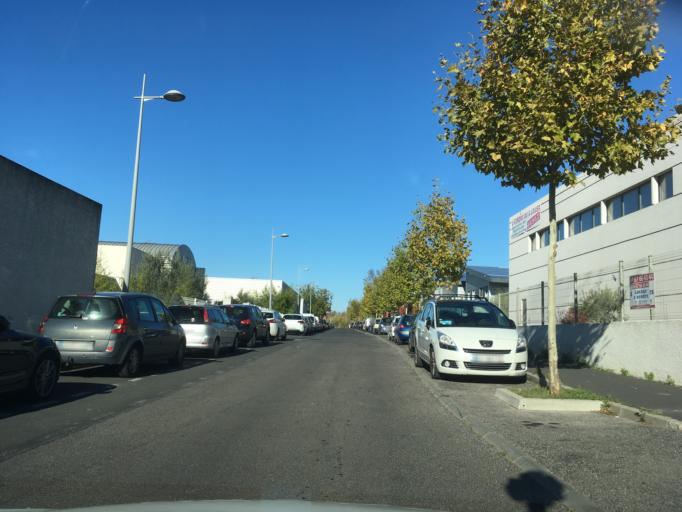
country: FR
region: Languedoc-Roussillon
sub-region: Departement de l'Herault
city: Juvignac
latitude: 43.6196
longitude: 3.8213
